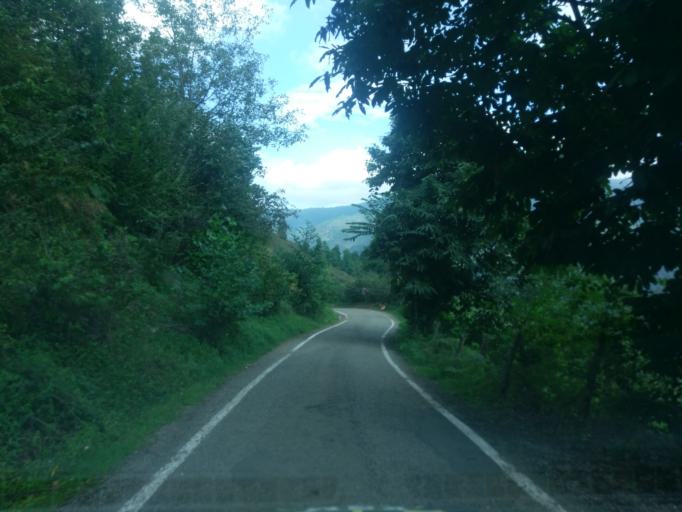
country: TR
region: Ordu
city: Camas
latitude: 40.9253
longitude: 37.6049
